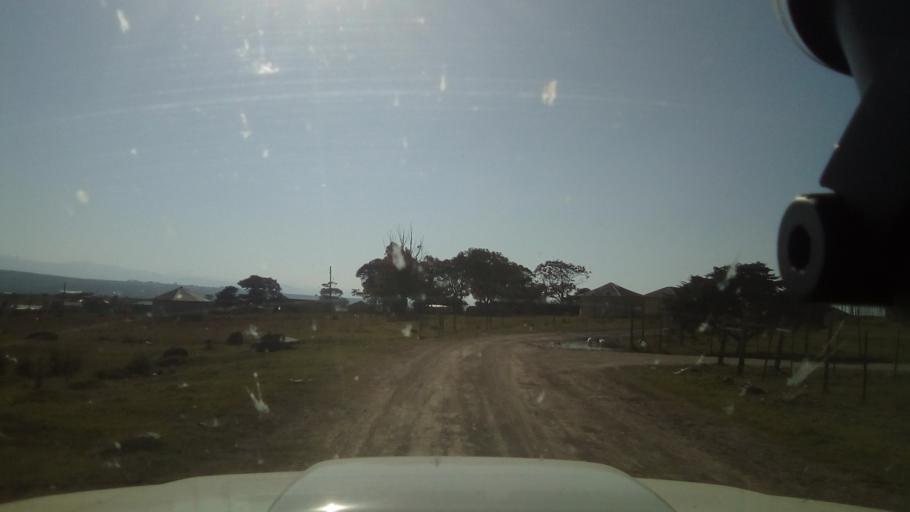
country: ZA
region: Eastern Cape
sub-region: Buffalo City Metropolitan Municipality
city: Bhisho
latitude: -32.9373
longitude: 27.3359
